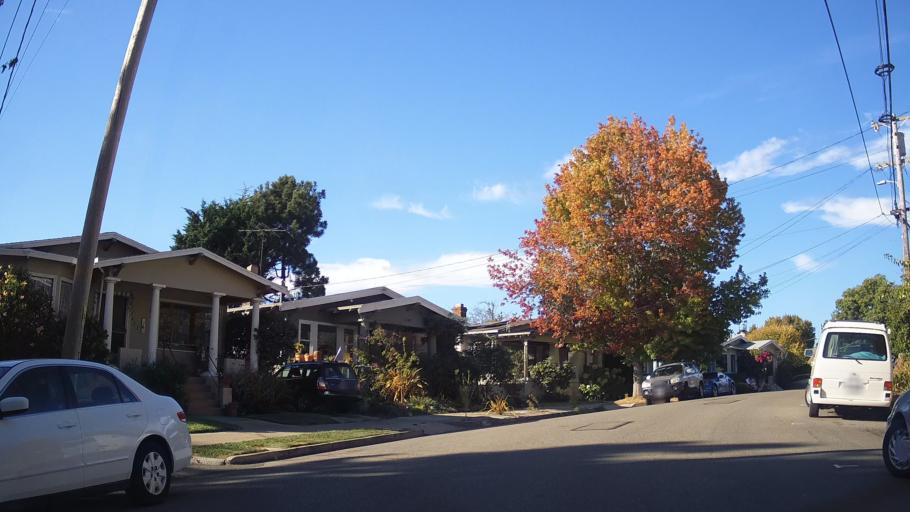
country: US
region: California
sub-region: Alameda County
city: Berkeley
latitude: 37.8829
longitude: -122.2806
